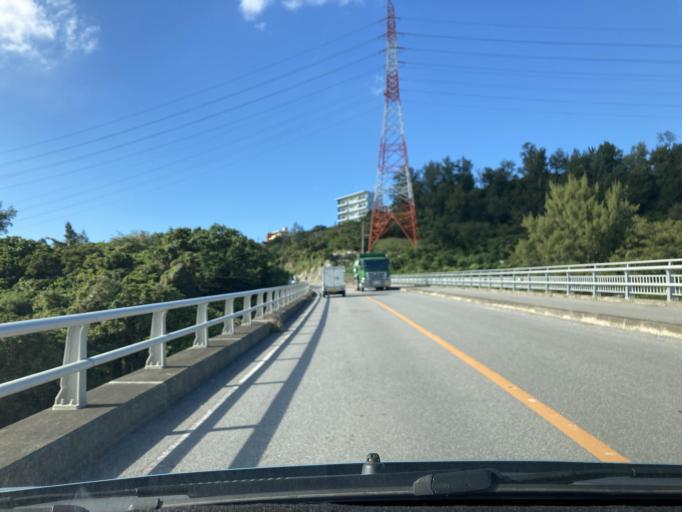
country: JP
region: Okinawa
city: Okinawa
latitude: 26.3391
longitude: 127.8340
